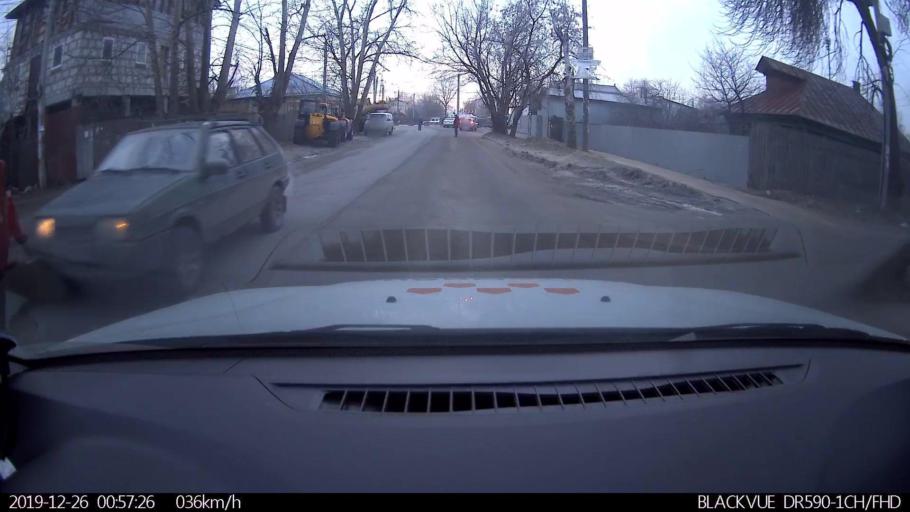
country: RU
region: Nizjnij Novgorod
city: Nizhniy Novgorod
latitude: 56.3012
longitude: 43.8761
